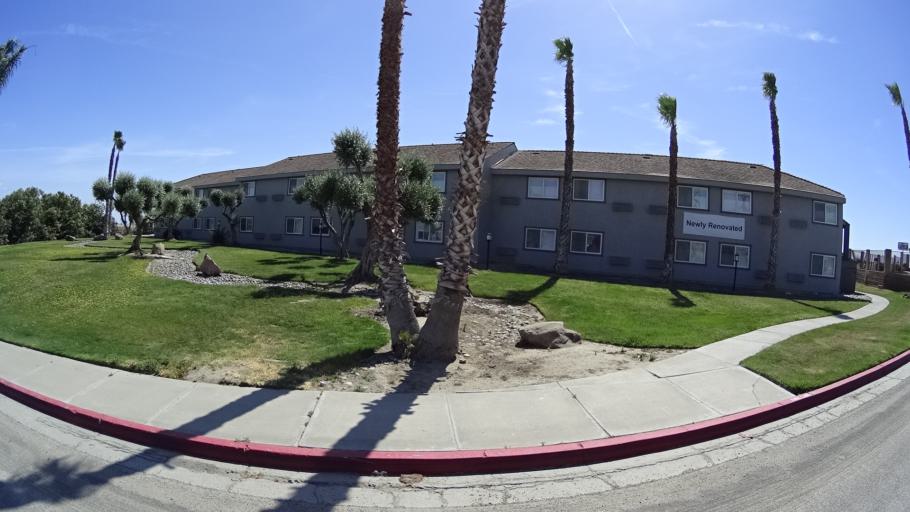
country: US
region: California
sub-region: Kings County
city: Kettleman City
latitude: 35.9871
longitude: -119.9616
